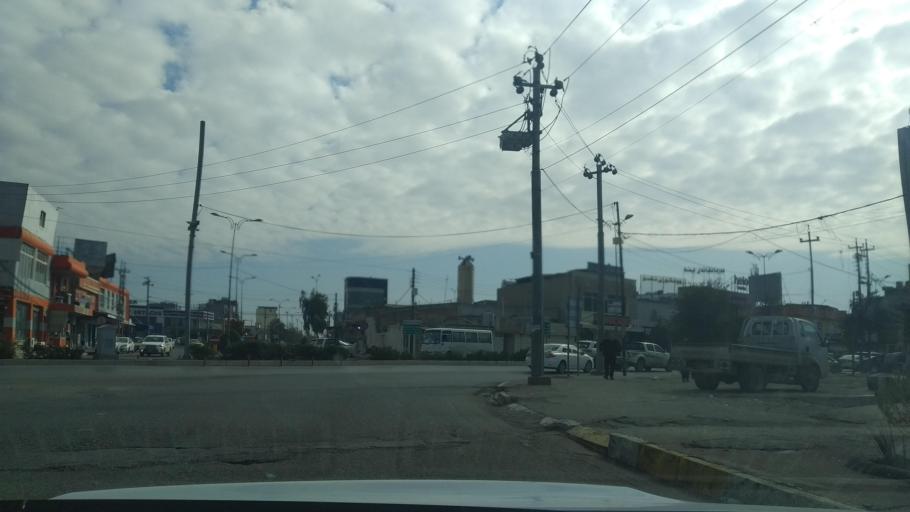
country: IQ
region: Arbil
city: Erbil
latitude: 36.1737
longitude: 44.0363
